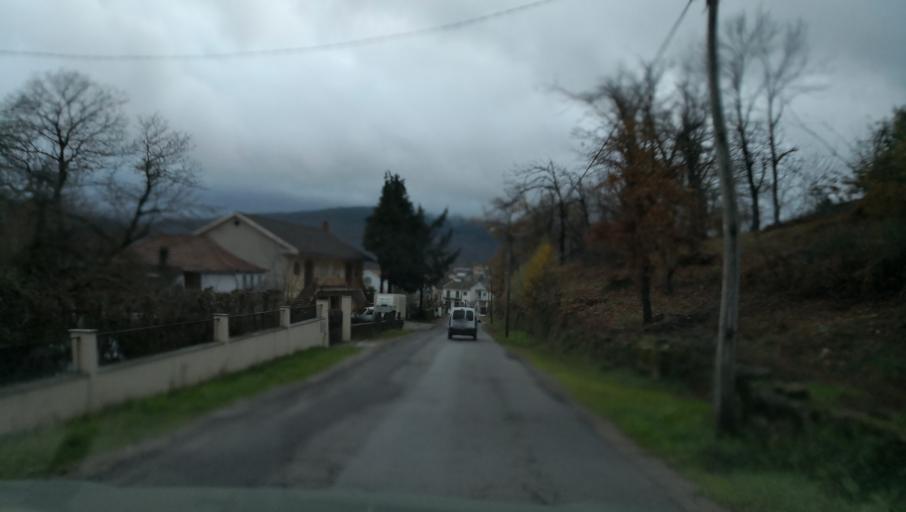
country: PT
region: Vila Real
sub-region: Santa Marta de Penaguiao
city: Santa Marta de Penaguiao
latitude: 41.3030
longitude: -7.8696
